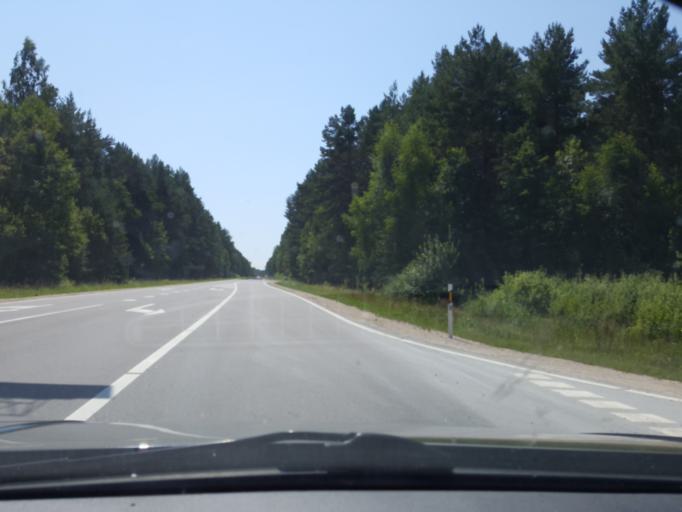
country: LV
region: Rucavas
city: Rucava
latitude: 56.1575
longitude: 21.1474
